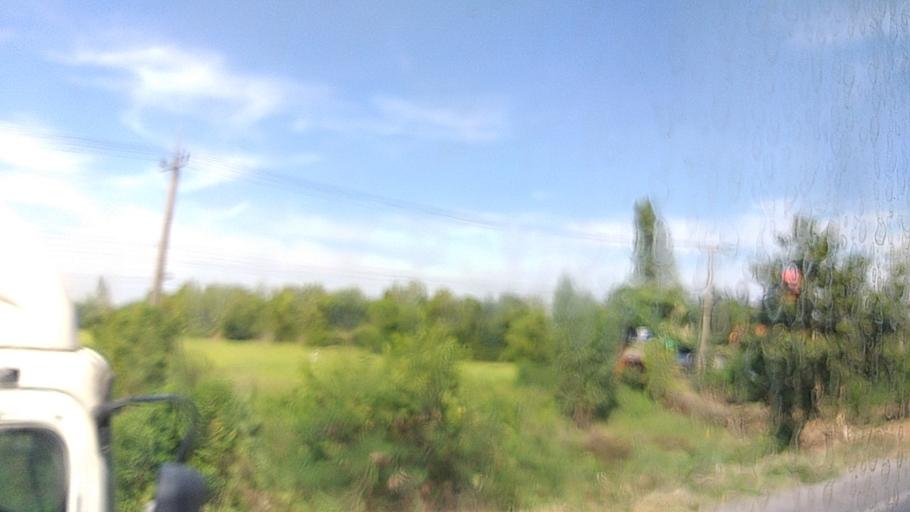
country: TH
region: Khon Kaen
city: Khon Kaen
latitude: 16.4276
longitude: 102.9172
